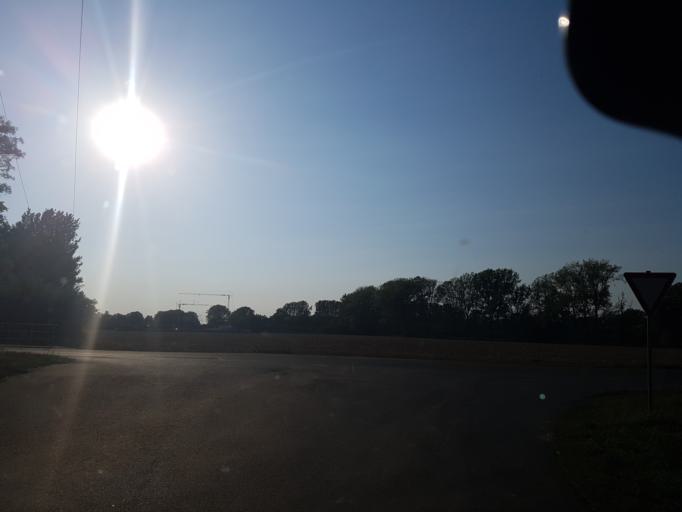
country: DE
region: Saxony
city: Stauchitz
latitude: 51.2562
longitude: 13.2285
